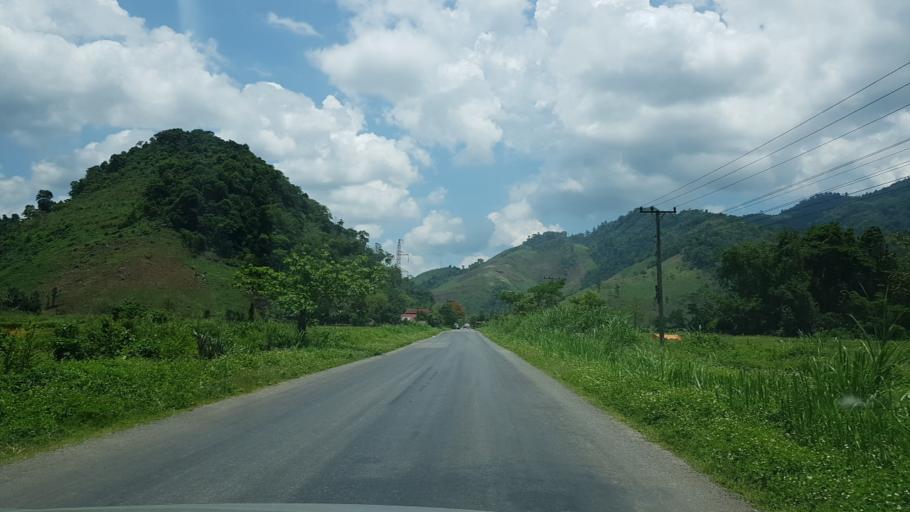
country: LA
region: Vientiane
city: Muang Kasi
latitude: 19.1306
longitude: 102.2737
